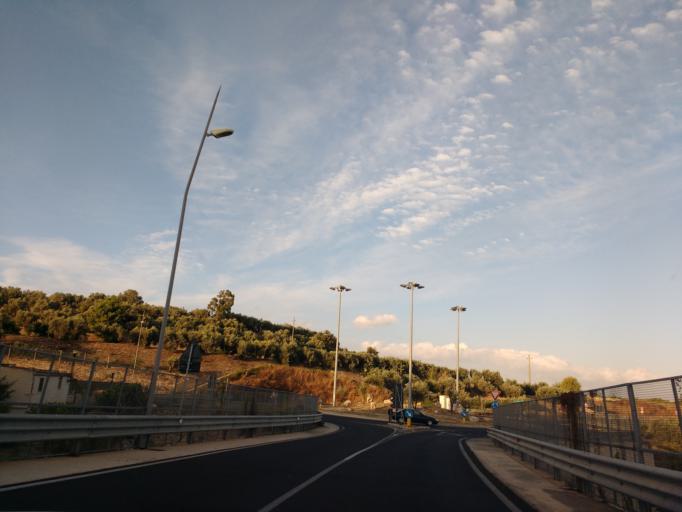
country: IT
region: Sicily
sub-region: Provincia di Siracusa
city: Noto
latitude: 36.8721
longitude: 15.0872
